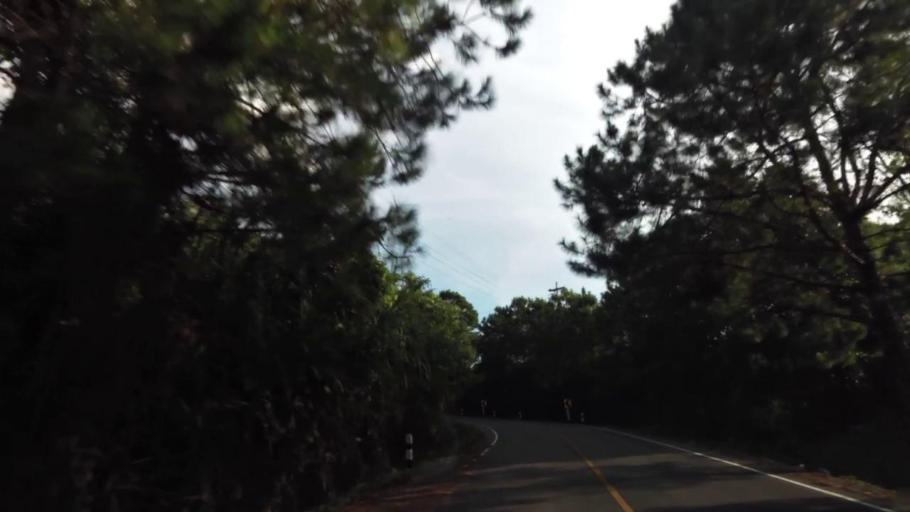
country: TH
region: Chiang Rai
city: Khun Tan
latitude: 19.8720
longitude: 100.3218
